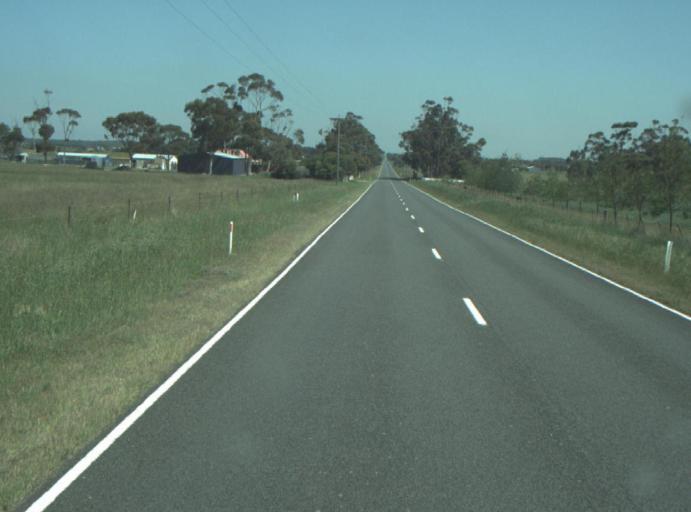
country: AU
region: Victoria
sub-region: Greater Geelong
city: Lara
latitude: -37.9692
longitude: 144.4060
